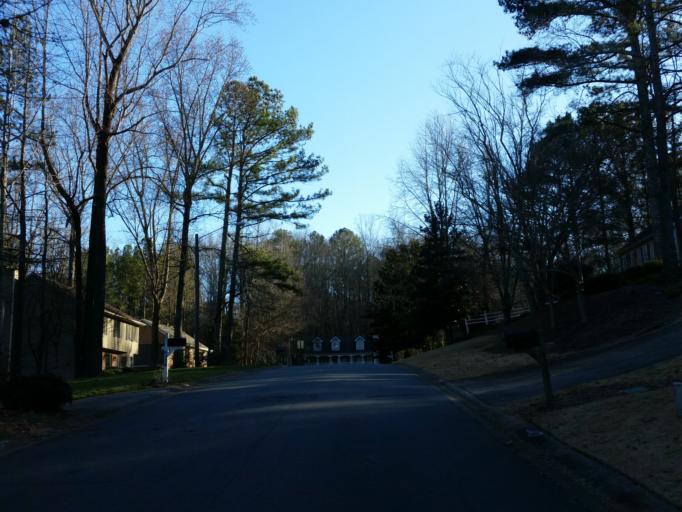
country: US
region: Georgia
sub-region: Cherokee County
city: Woodstock
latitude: 34.0540
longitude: -84.4741
